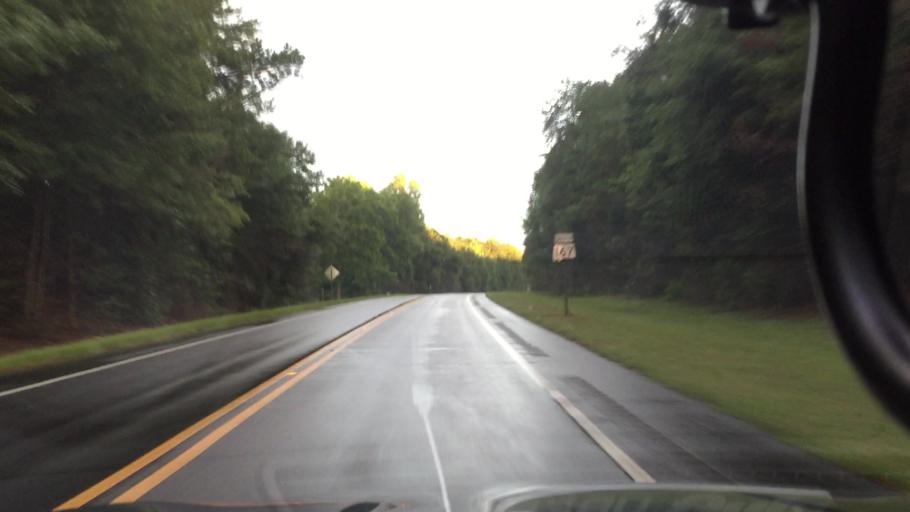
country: US
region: Alabama
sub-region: Pike County
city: Brundidge
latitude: 31.5762
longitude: -85.9306
